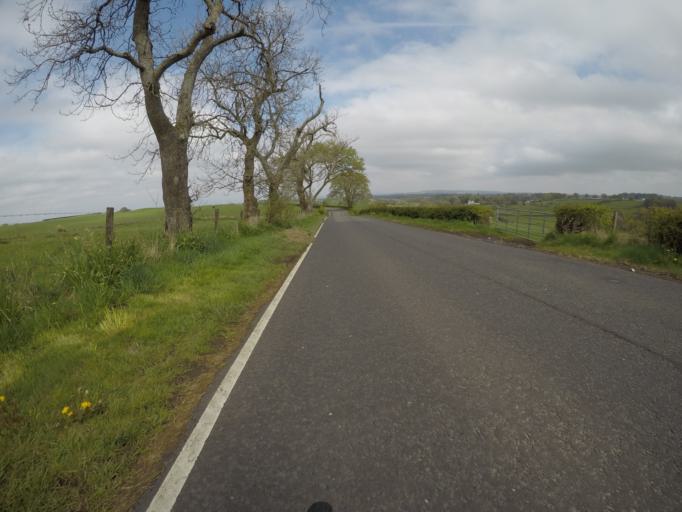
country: GB
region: Scotland
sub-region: East Renfrewshire
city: Barrhead
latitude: 55.7700
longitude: -4.3717
